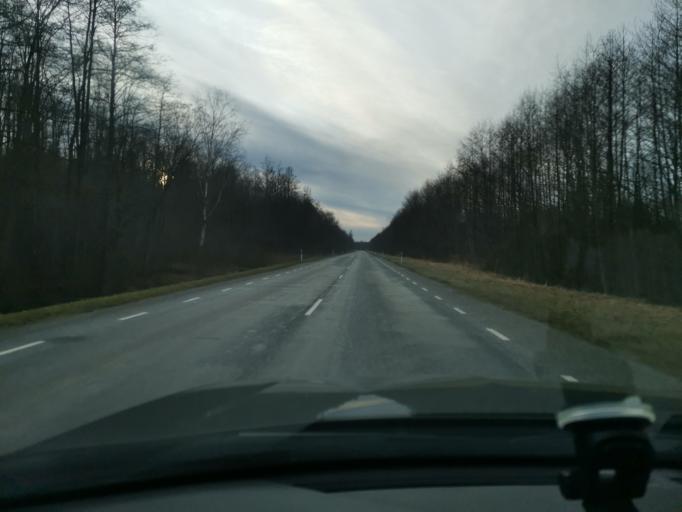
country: EE
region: Ida-Virumaa
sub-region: Narva-Joesuu linn
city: Narva-Joesuu
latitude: 59.3271
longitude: 27.9316
